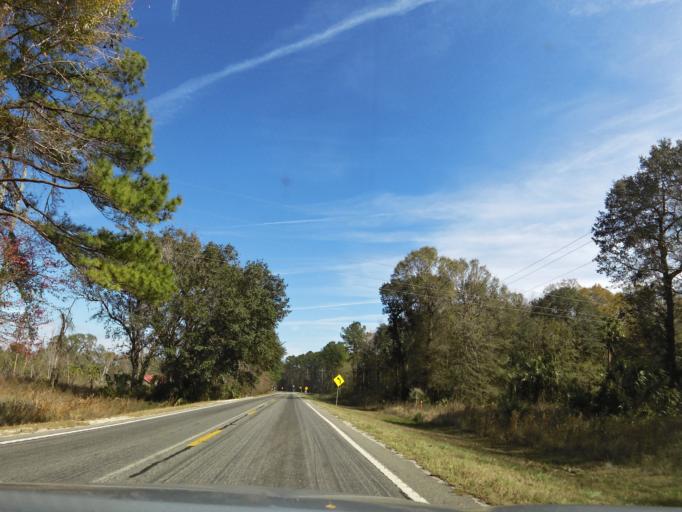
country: US
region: Georgia
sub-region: Glynn County
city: Dock Junction
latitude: 31.2526
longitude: -81.6089
